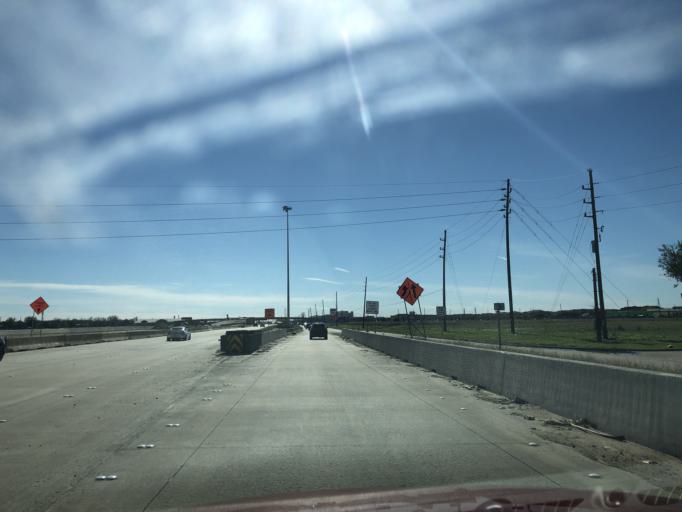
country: US
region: Texas
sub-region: Brazoria County
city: Brookside Village
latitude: 29.5762
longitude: -95.3865
